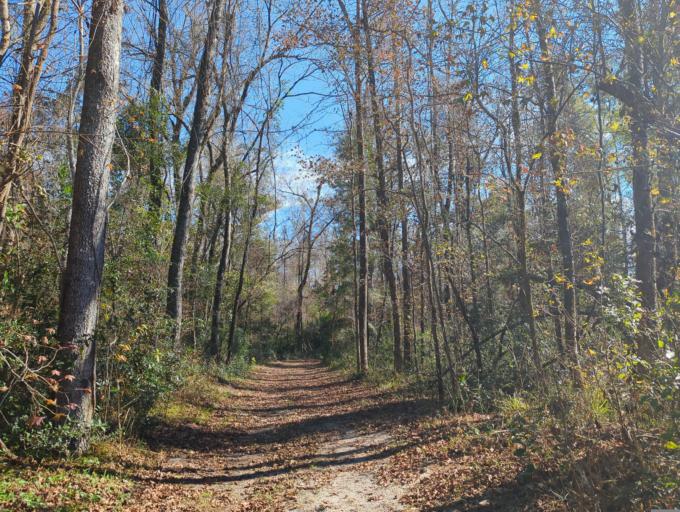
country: US
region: Florida
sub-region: Wakulla County
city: Crawfordville
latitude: 30.1874
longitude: -84.3259
